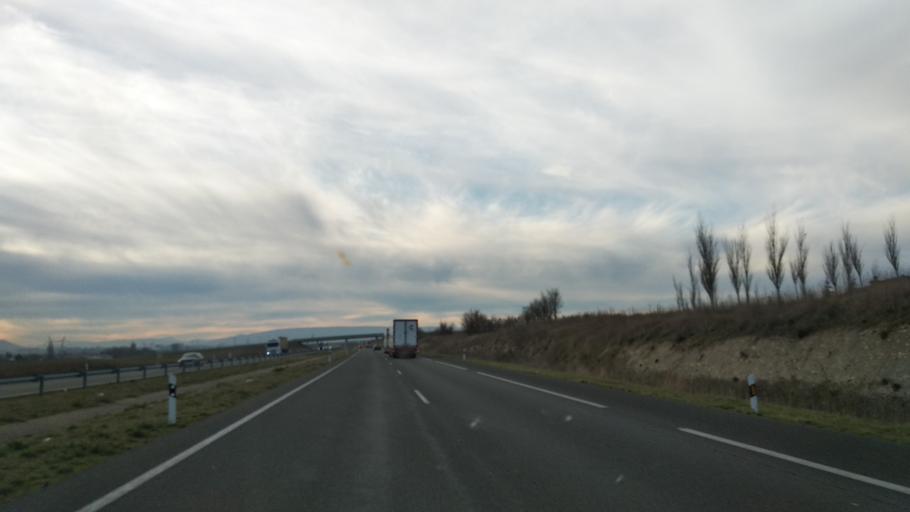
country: ES
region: Basque Country
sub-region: Provincia de Alava
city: Gasteiz / Vitoria
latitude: 42.8788
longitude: -2.5788
